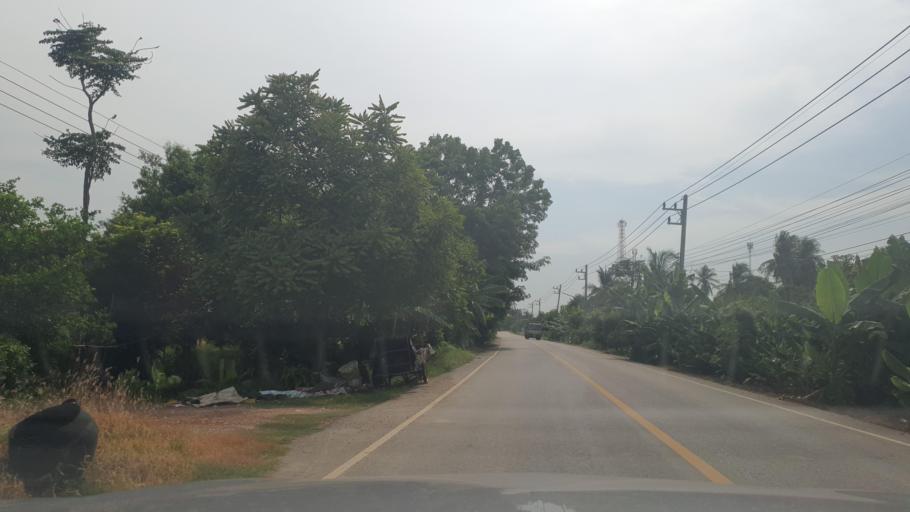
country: TH
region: Sukhothai
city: Si Samrong
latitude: 17.1210
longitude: 99.8551
